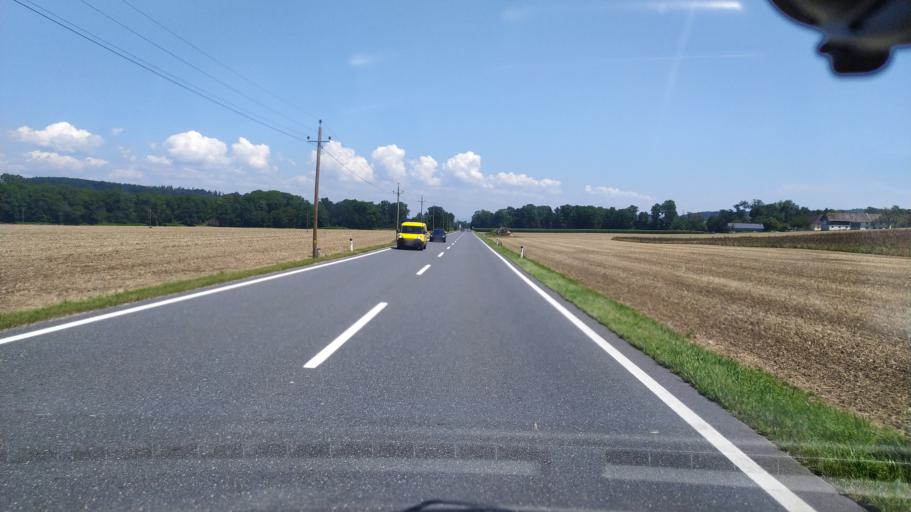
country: AT
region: Upper Austria
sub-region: Politischer Bezirk Linz-Land
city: Sankt Florian
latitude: 48.1935
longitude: 14.3522
